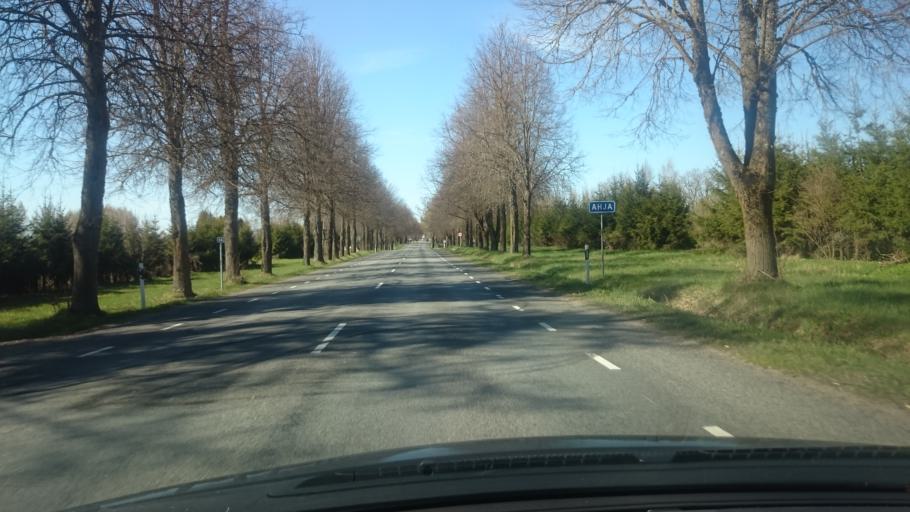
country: EE
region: Polvamaa
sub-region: Polva linn
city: Polva
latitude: 58.1981
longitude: 27.0783
